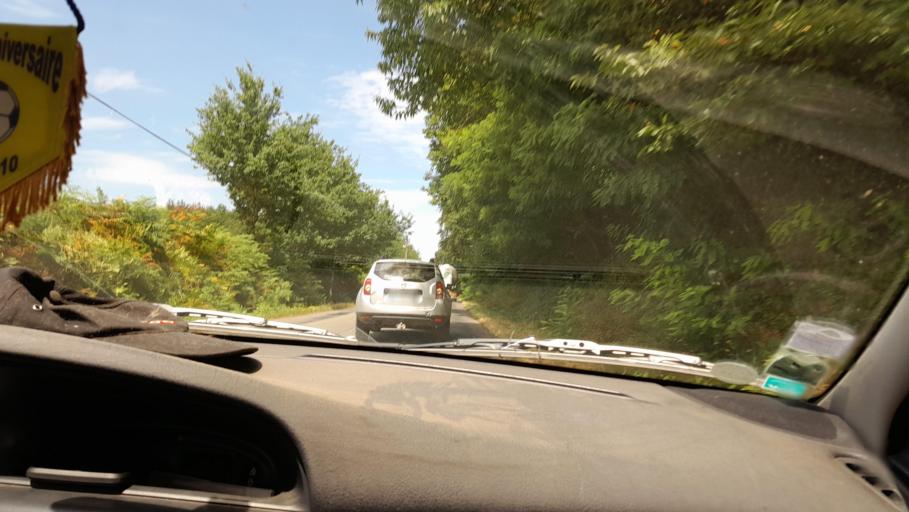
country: FR
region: Brittany
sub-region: Departement d'Ille-et-Vilaine
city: Luitre
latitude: 48.2730
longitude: -1.1490
